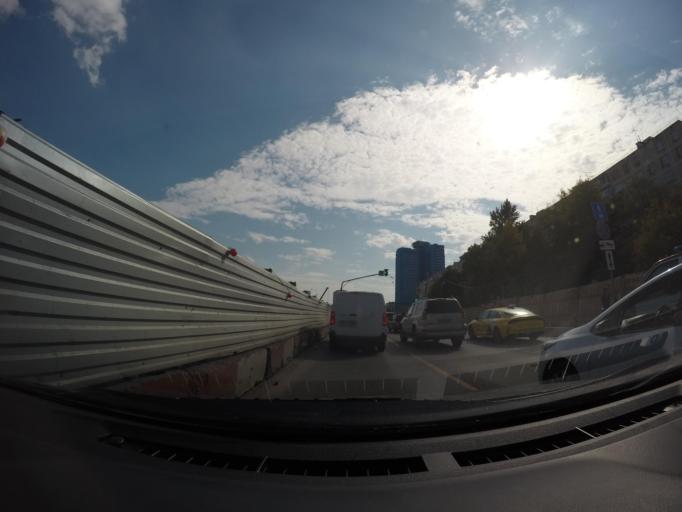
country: RU
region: Moscow
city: Likhobory
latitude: 55.8297
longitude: 37.5726
